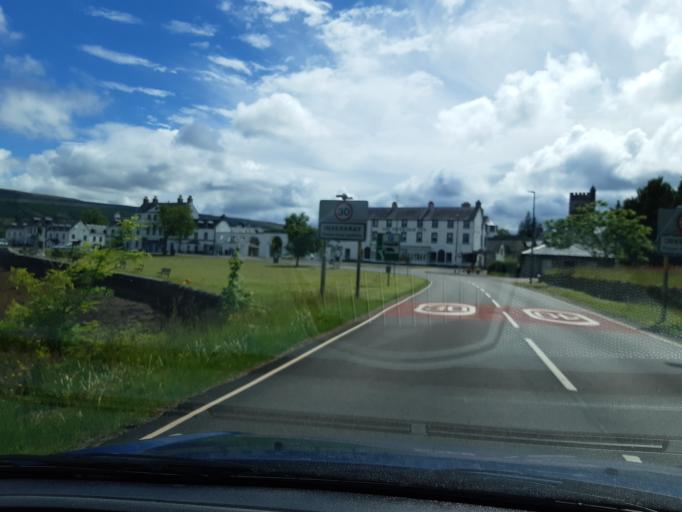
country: GB
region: Scotland
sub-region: Argyll and Bute
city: Garelochhead
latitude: 56.2328
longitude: -5.0738
